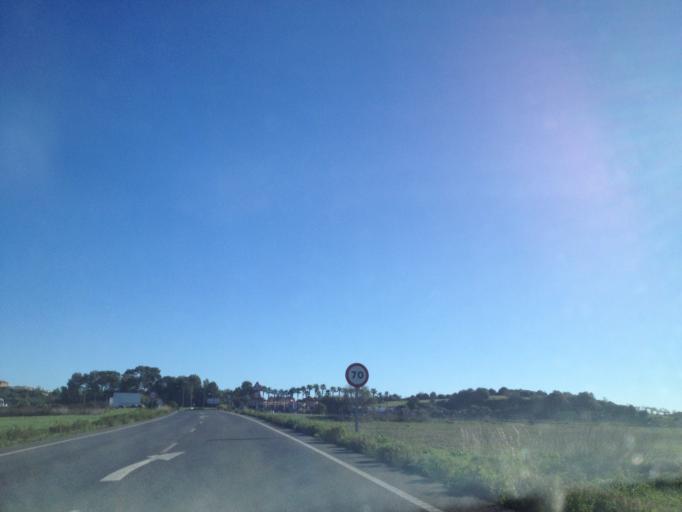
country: ES
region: Balearic Islands
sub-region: Illes Balears
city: Ariany
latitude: 39.6458
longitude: 3.0962
